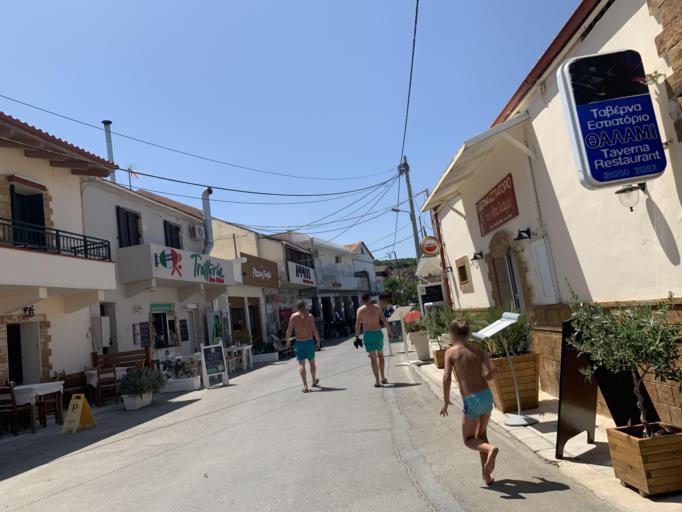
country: GR
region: Crete
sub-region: Nomos Chanias
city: Kalivai
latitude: 35.4493
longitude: 24.1994
